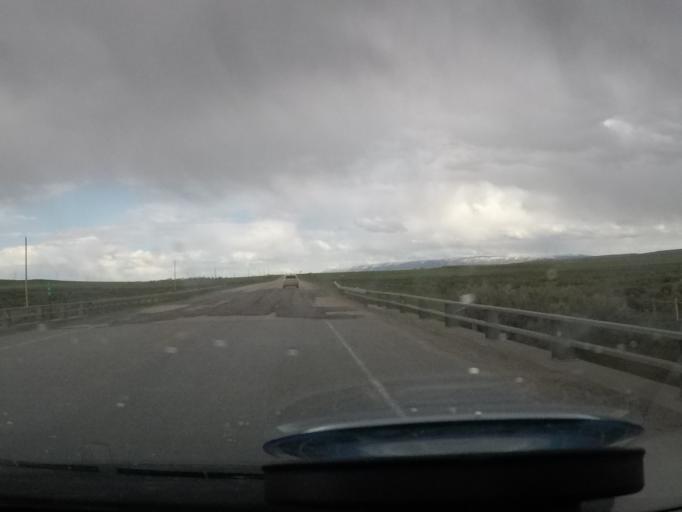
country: US
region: Wyoming
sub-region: Natrona County
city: Mills
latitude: 42.9590
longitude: -106.6562
